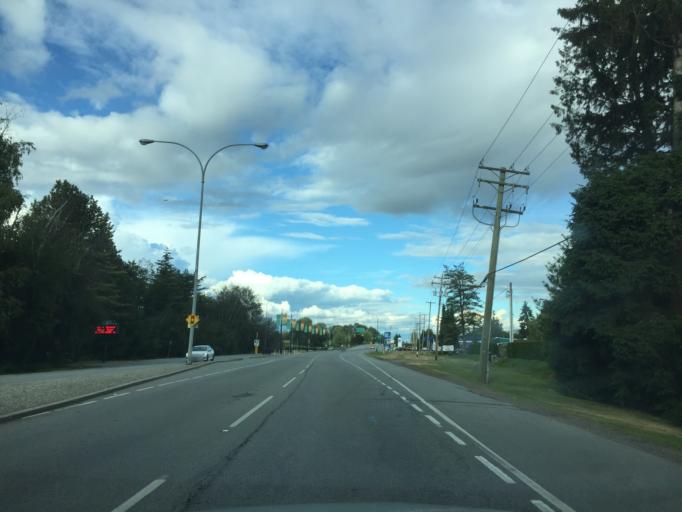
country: CA
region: British Columbia
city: Richmond
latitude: 49.1700
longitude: -123.0952
